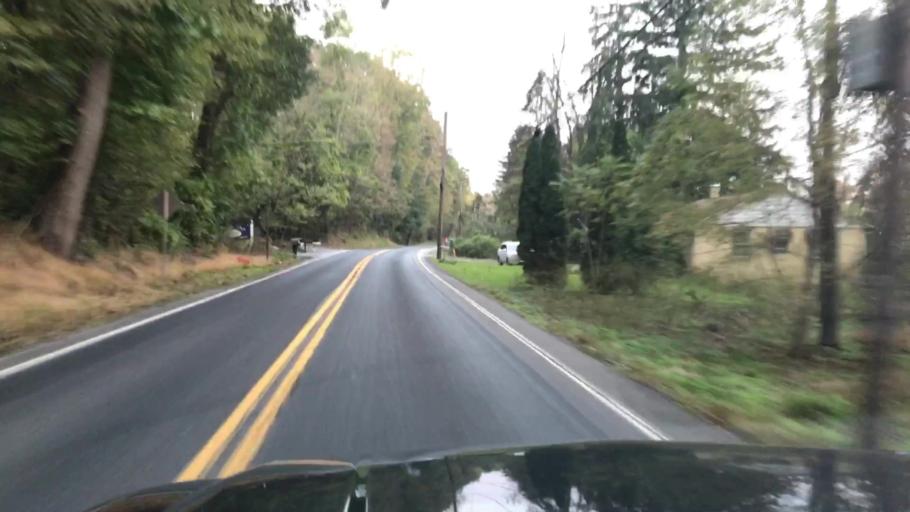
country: US
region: Pennsylvania
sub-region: Cumberland County
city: Shiremanstown
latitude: 40.1776
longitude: -76.9258
